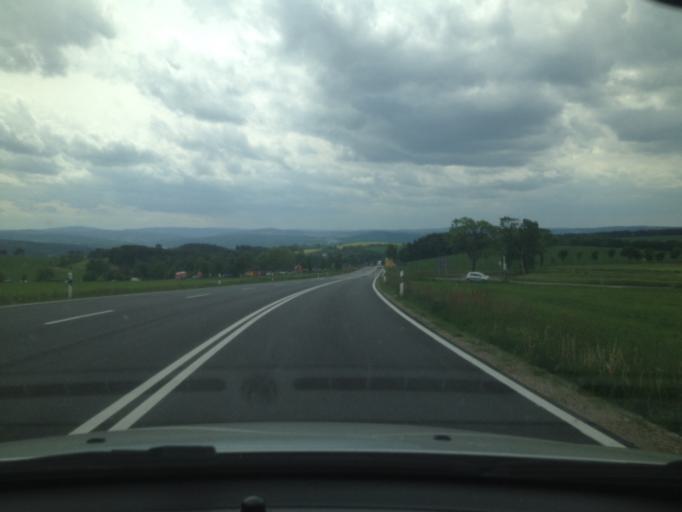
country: DE
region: Saxony
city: Lossnitz
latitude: 50.6491
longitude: 12.7489
